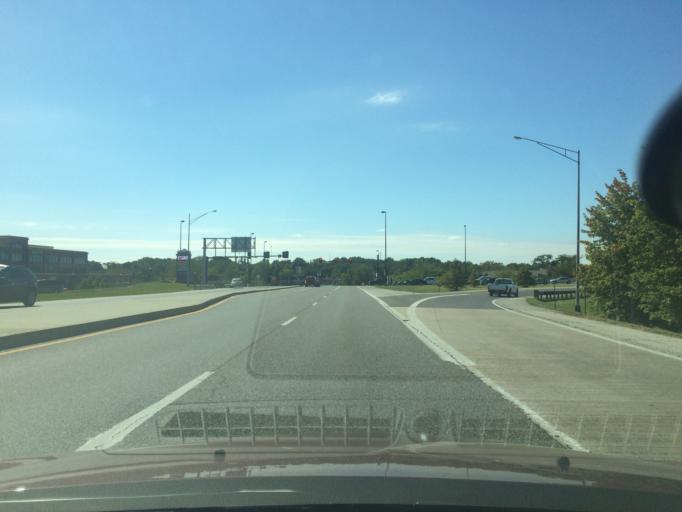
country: US
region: Missouri
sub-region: Saint Charles County
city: Saint Charles
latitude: 38.7682
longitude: -90.4947
